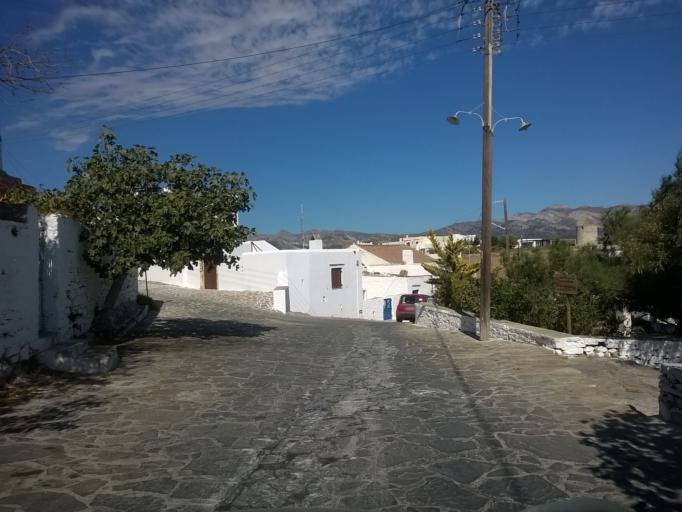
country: GR
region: South Aegean
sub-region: Nomos Kykladon
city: Filotion
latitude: 37.0402
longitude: 25.4347
